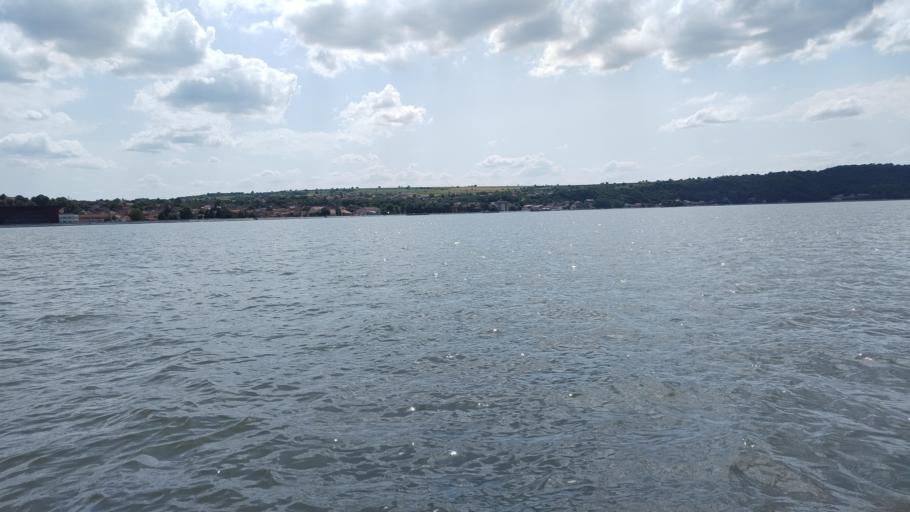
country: RS
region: Central Serbia
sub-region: Branicevski Okrug
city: Golubac
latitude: 44.6586
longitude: 21.6411
